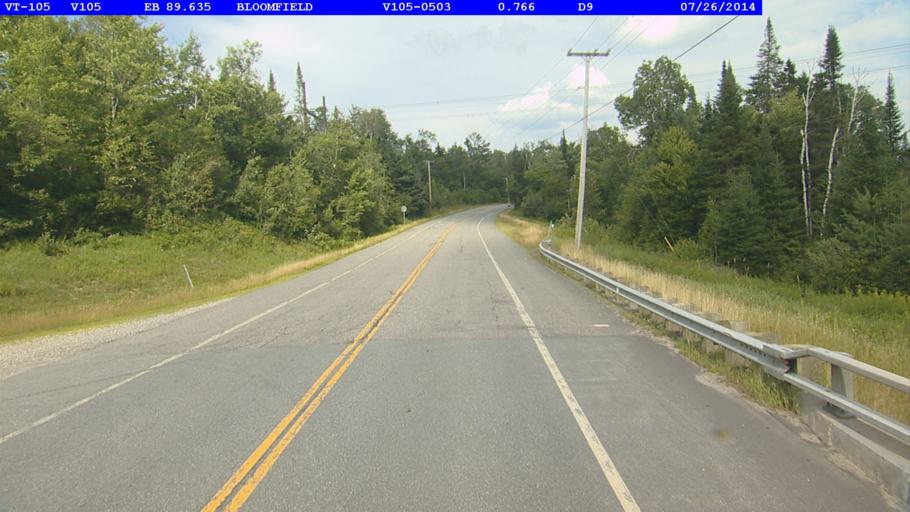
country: US
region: New Hampshire
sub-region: Coos County
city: Stratford
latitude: 44.7791
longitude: -71.6761
